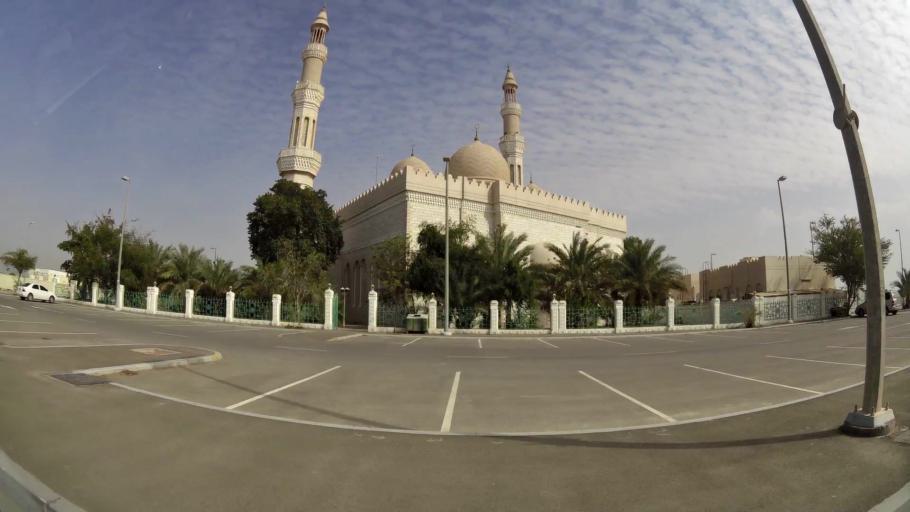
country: AE
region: Abu Dhabi
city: Abu Dhabi
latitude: 24.5929
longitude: 54.7005
